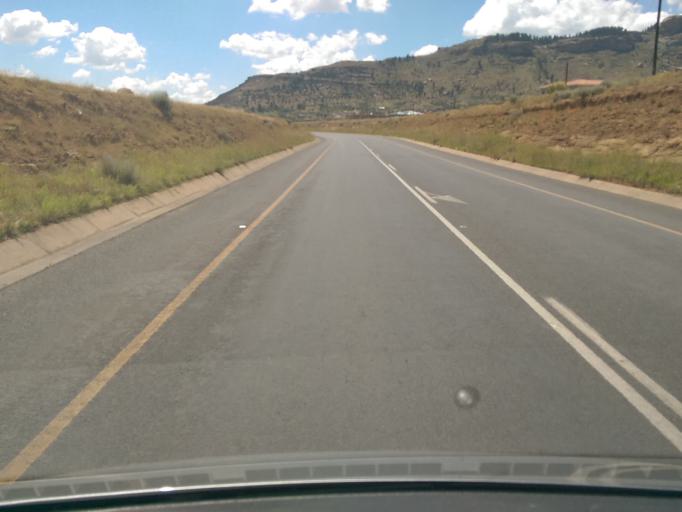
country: LS
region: Maseru
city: Maseru
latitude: -29.3704
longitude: 27.4745
